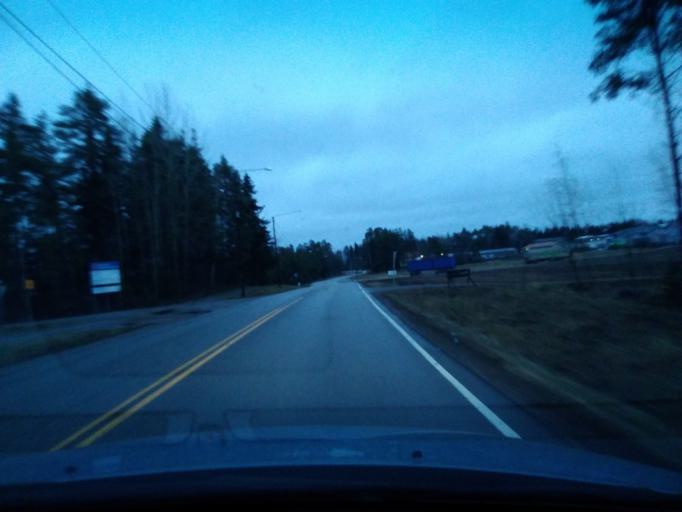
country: FI
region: Uusimaa
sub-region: Porvoo
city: Askola
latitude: 60.4998
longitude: 25.5584
